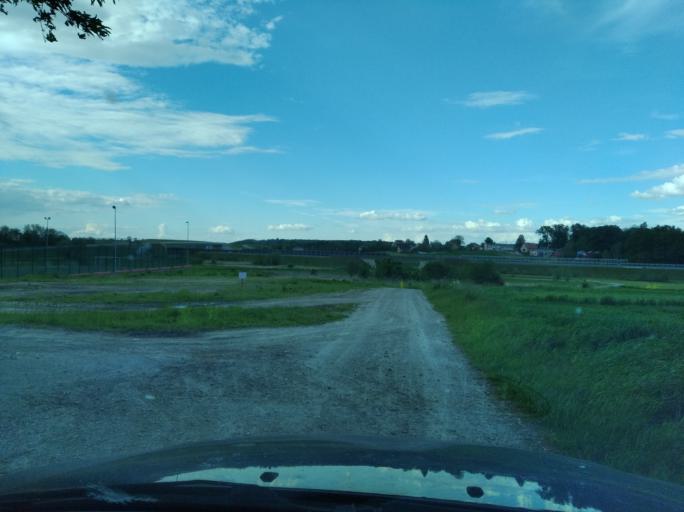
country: PL
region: Subcarpathian Voivodeship
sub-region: Powiat jaroslawski
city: Rokietnica
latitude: 49.9400
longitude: 22.6685
